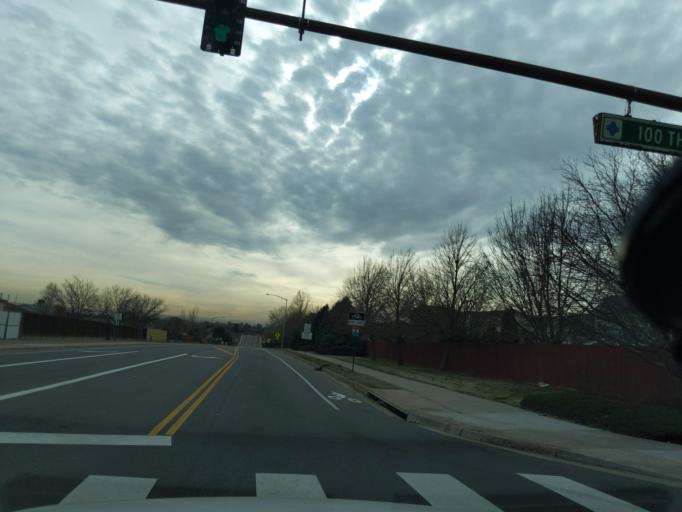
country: US
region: Colorado
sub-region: Adams County
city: Thornton
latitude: 39.8778
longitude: -104.9590
